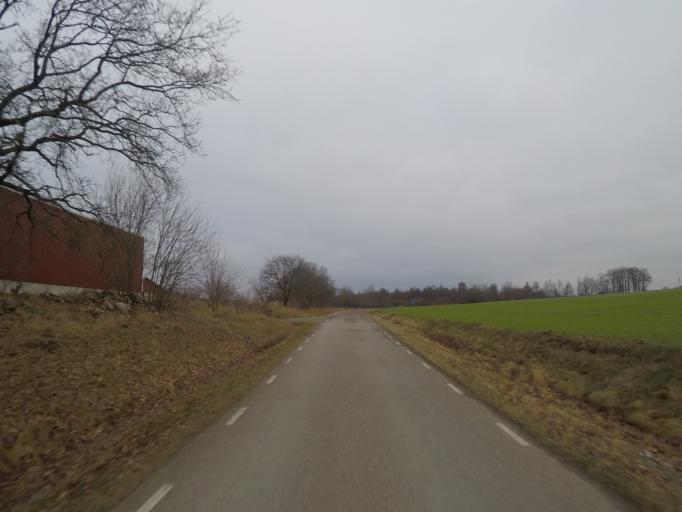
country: SE
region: Skane
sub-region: Hoors Kommun
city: Loberod
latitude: 55.7920
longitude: 13.4032
